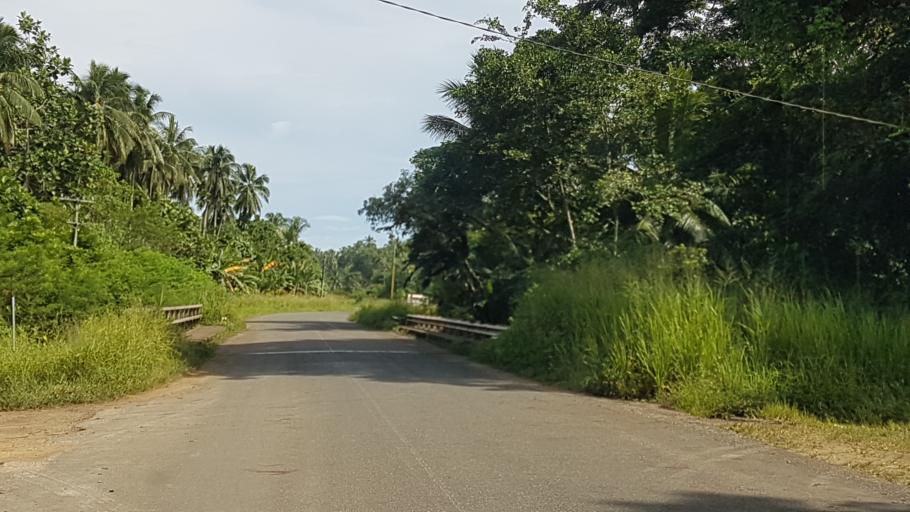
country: PG
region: Madang
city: Madang
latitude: -5.0119
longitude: 145.7917
